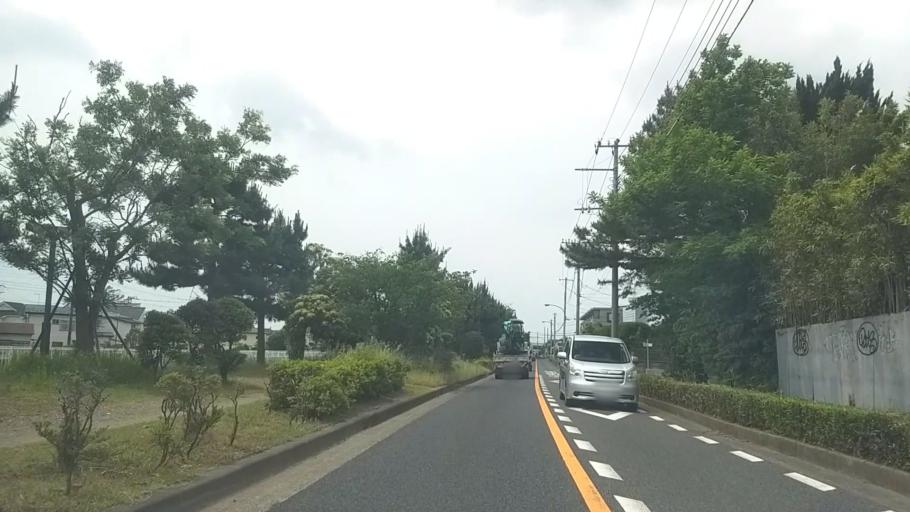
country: JP
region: Kanagawa
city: Fujisawa
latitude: 35.3317
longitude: 139.4668
